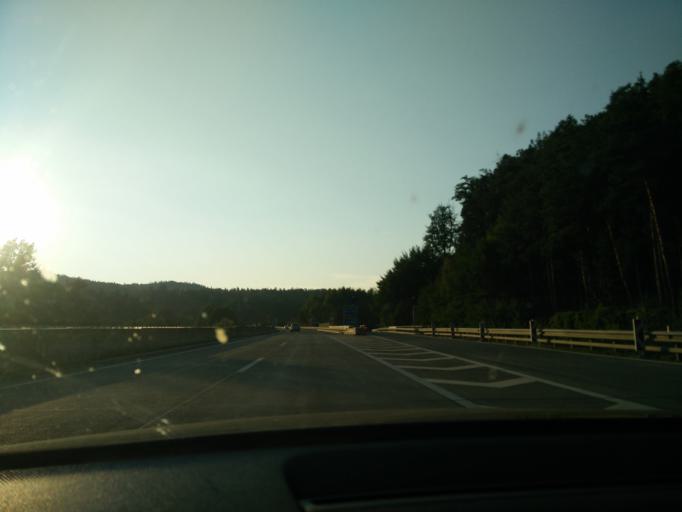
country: AT
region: Carinthia
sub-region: Klagenfurt am Woerthersee
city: Klagenfurt am Woerthersee
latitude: 46.6280
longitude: 14.2437
